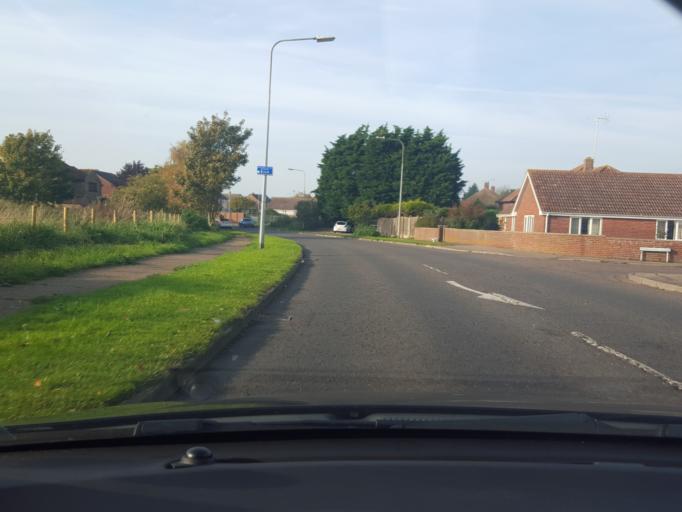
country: GB
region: England
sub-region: Essex
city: Dovercourt
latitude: 51.9274
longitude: 1.2457
